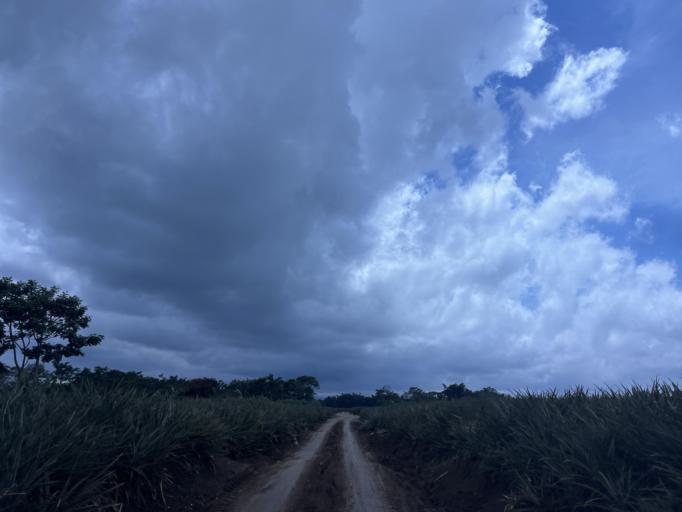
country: PH
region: Northern Mindanao
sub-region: Province of Bukidnon
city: Sumilao
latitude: 8.2970
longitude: 124.9242
